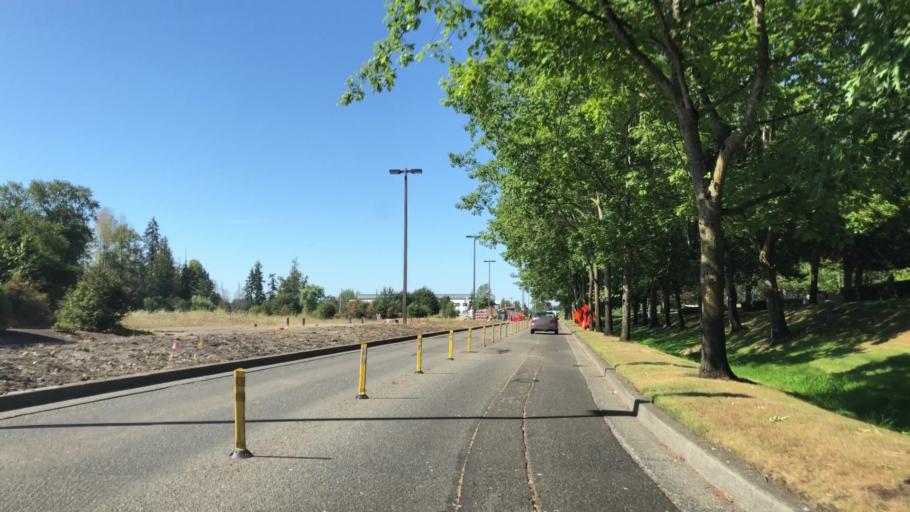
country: US
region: Washington
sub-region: Snohomish County
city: North Creek
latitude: 47.7997
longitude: -122.2063
